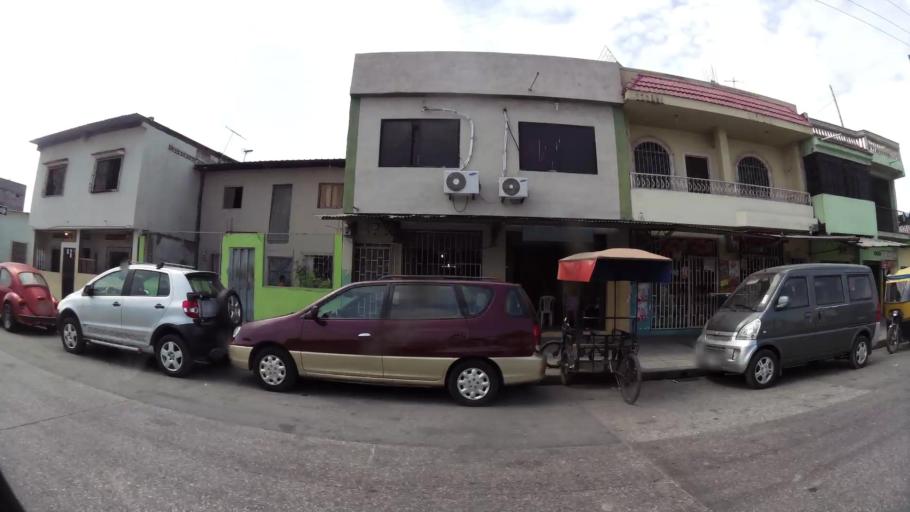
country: EC
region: Guayas
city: Guayaquil
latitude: -2.2825
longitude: -79.8835
